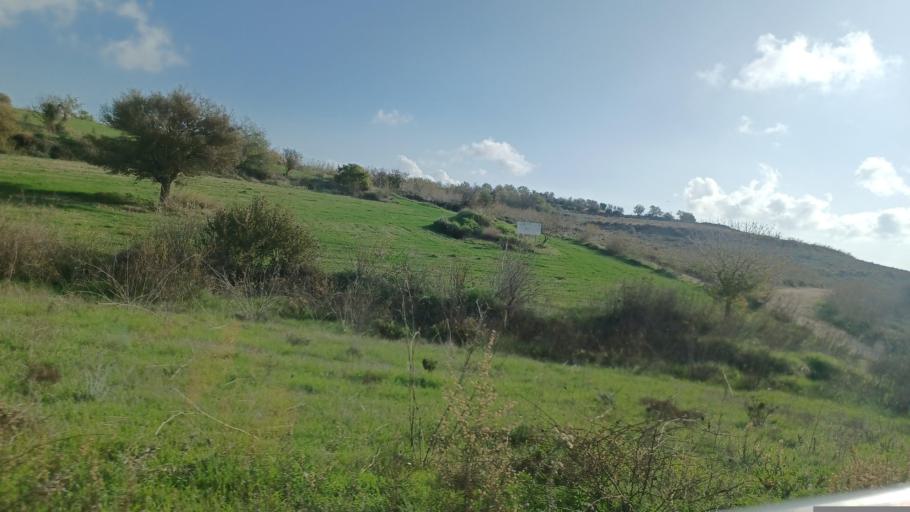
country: CY
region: Pafos
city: Mesogi
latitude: 34.8140
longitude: 32.4882
